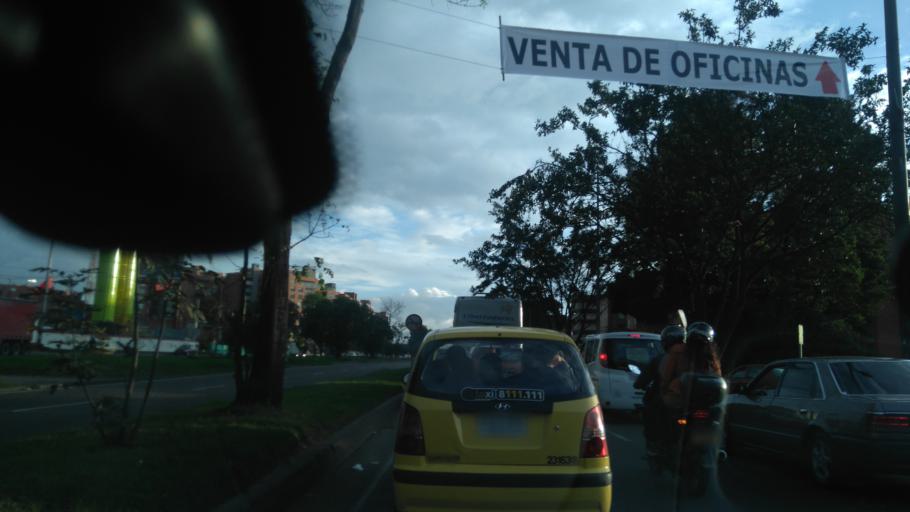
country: CO
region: Bogota D.C.
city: Bogota
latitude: 4.6656
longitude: -74.1126
